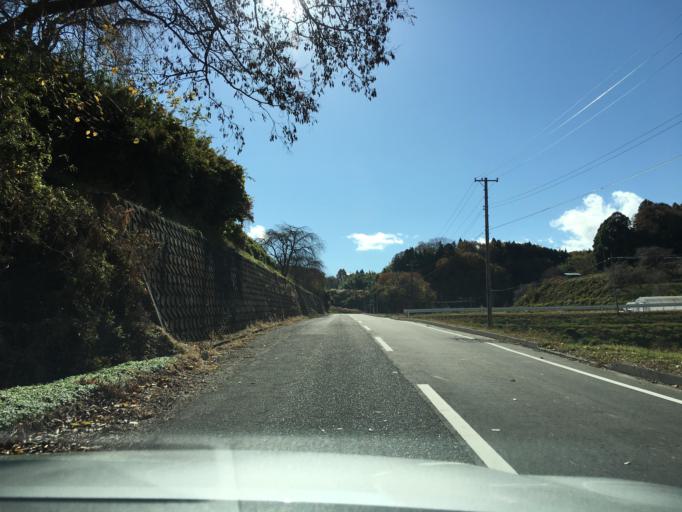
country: JP
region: Fukushima
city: Miharu
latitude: 37.4553
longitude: 140.4568
